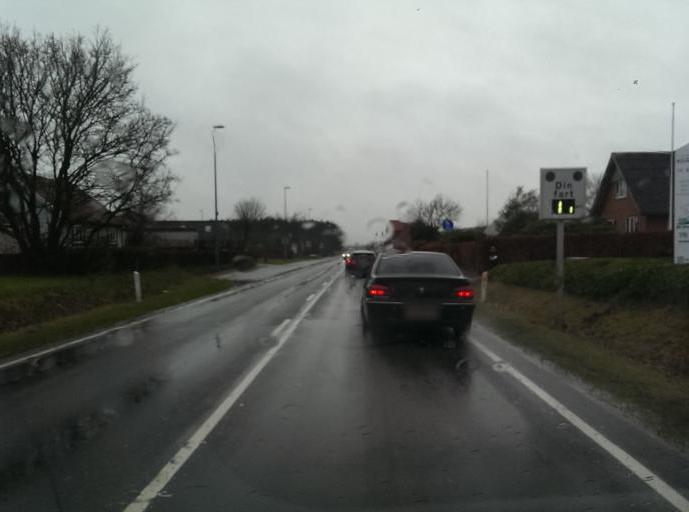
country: DK
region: South Denmark
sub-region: Varde Kommune
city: Olgod
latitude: 55.7150
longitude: 8.6102
